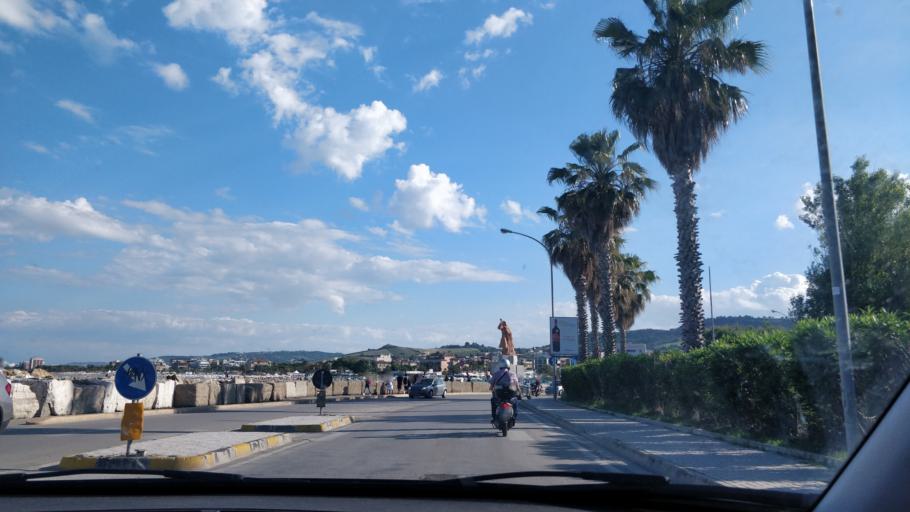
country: IT
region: The Marches
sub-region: Provincia di Ascoli Piceno
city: Grottammare
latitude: 42.9516
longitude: 13.8891
